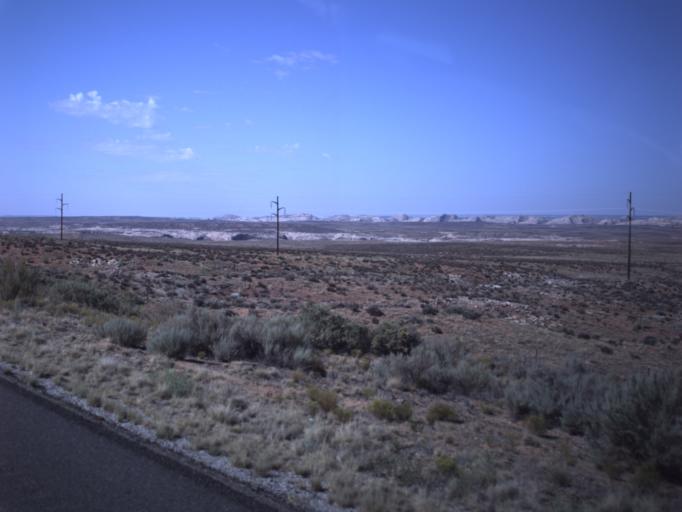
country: US
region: Utah
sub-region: San Juan County
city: Blanding
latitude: 37.3569
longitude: -109.5164
